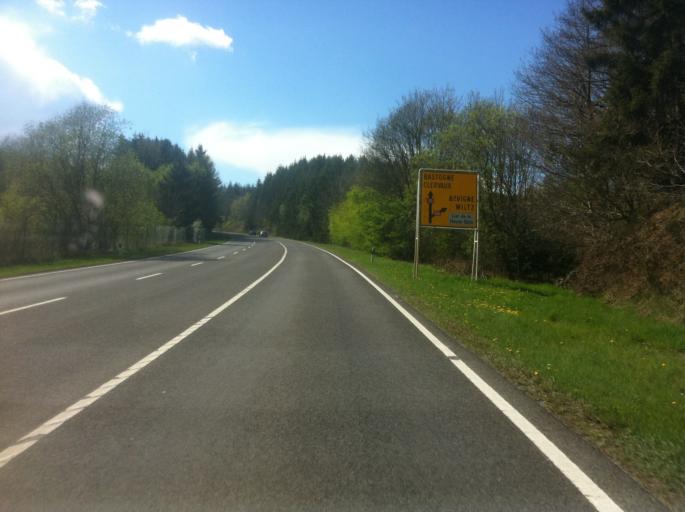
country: LU
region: Diekirch
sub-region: Canton de Wiltz
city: Winseler
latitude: 49.9468
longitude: 5.8908
